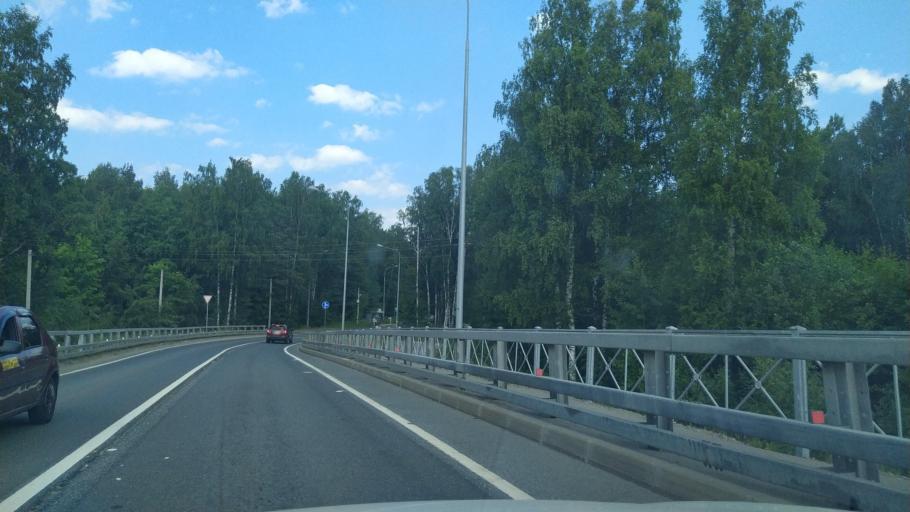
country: RU
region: St.-Petersburg
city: Kronshtadt
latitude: 60.0147
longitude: 29.7151
